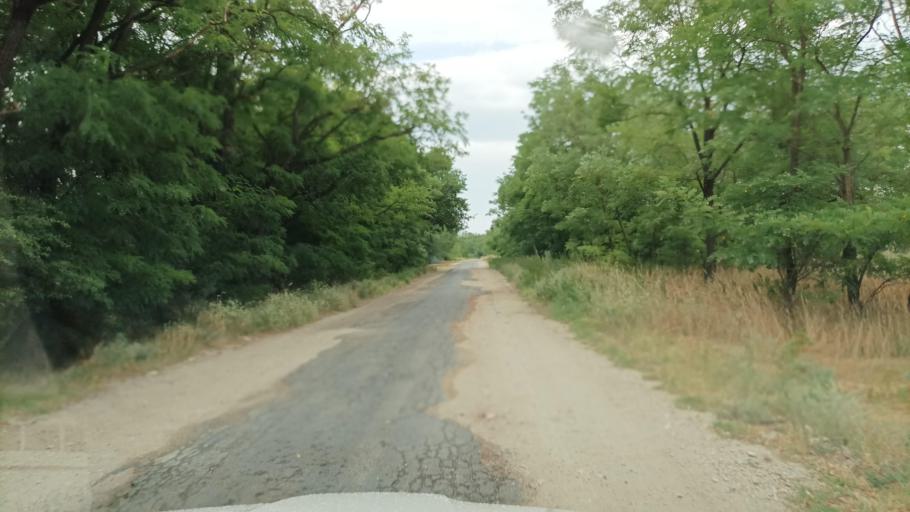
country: HU
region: Pest
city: Orkeny
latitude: 47.0291
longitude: 19.3651
